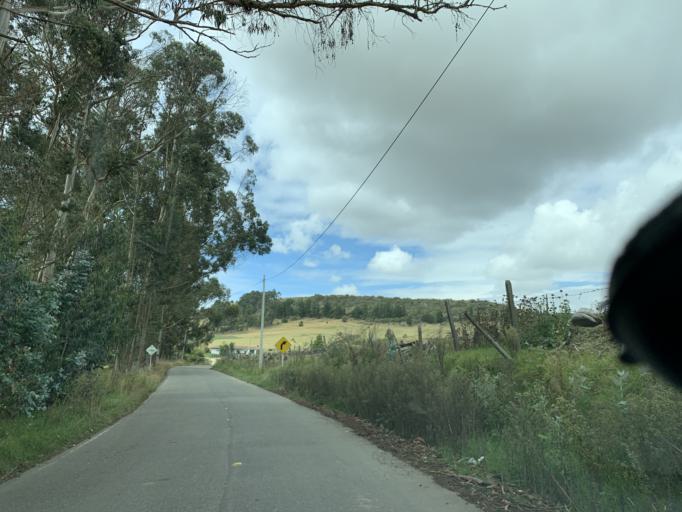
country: CO
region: Boyaca
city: Toca
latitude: 5.5719
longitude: -73.2248
